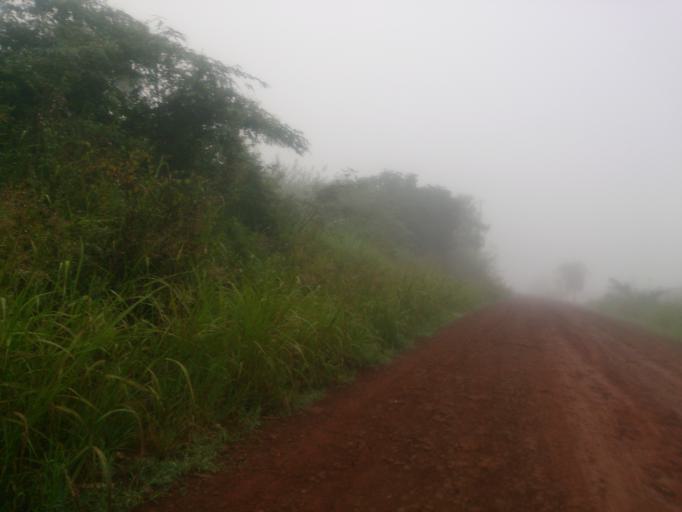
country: AR
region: Misiones
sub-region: Departamento de Obera
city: Obera
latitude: -27.4707
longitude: -55.1063
